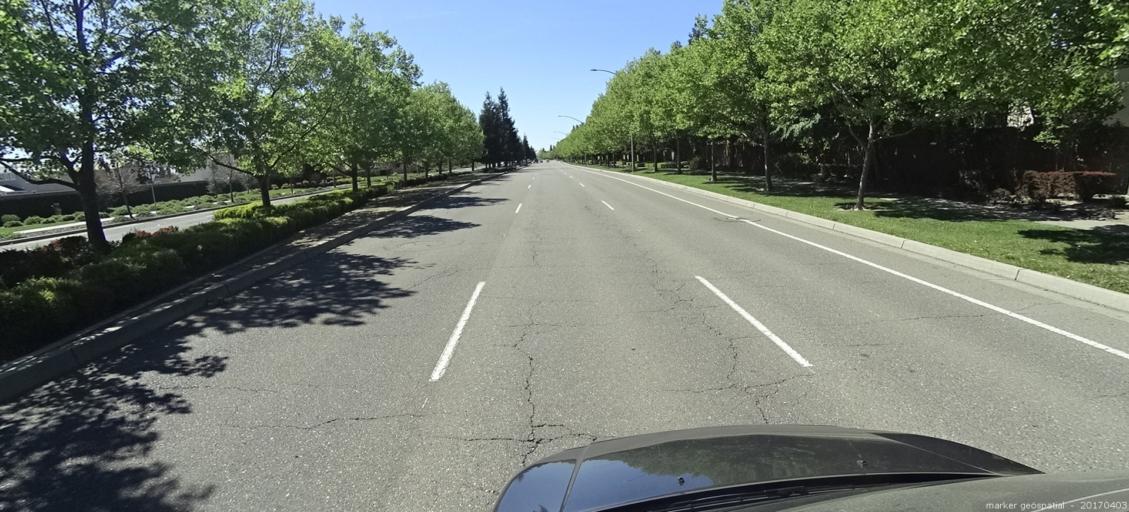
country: US
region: California
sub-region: Sacramento County
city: Rio Linda
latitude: 38.6563
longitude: -121.4988
